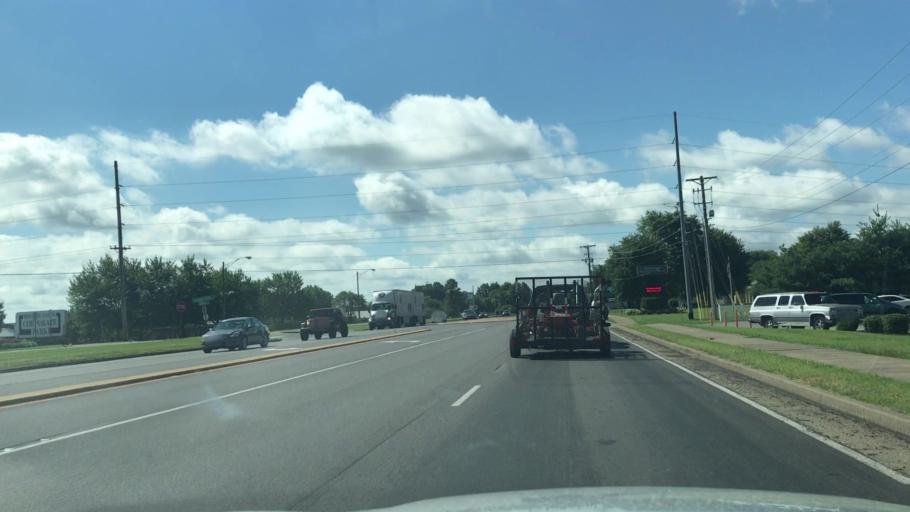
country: US
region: Kentucky
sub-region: Warren County
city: Plano
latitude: 36.9265
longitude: -86.4116
